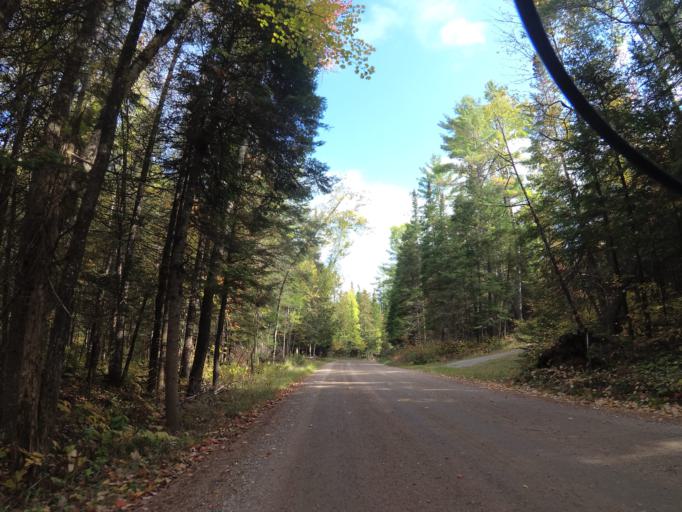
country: CA
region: Ontario
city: Pembroke
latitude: 45.2656
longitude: -77.2116
